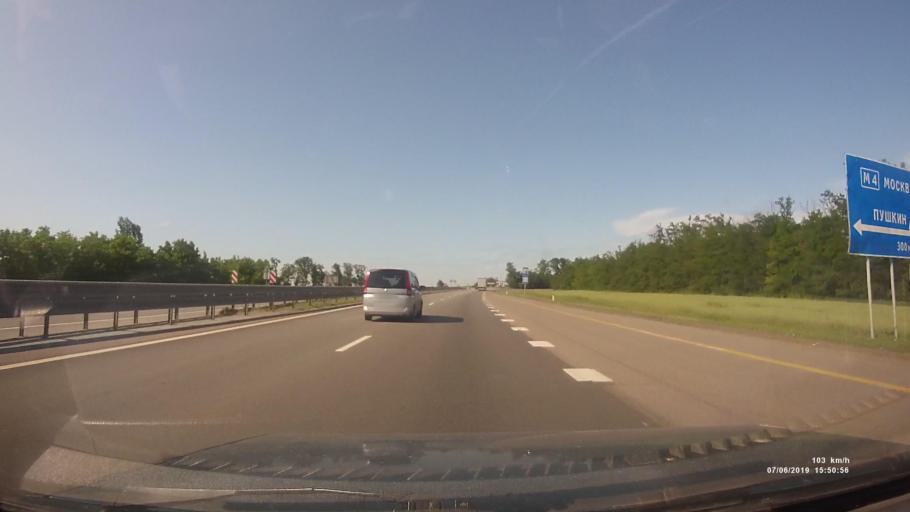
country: RU
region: Rostov
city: Gornyy
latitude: 47.8125
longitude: 40.1734
